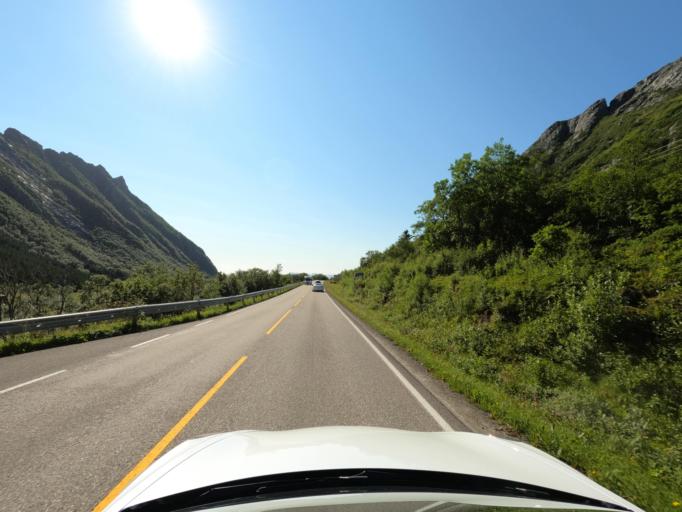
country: NO
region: Nordland
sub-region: Vagan
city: Kabelvag
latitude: 68.2073
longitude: 14.2495
